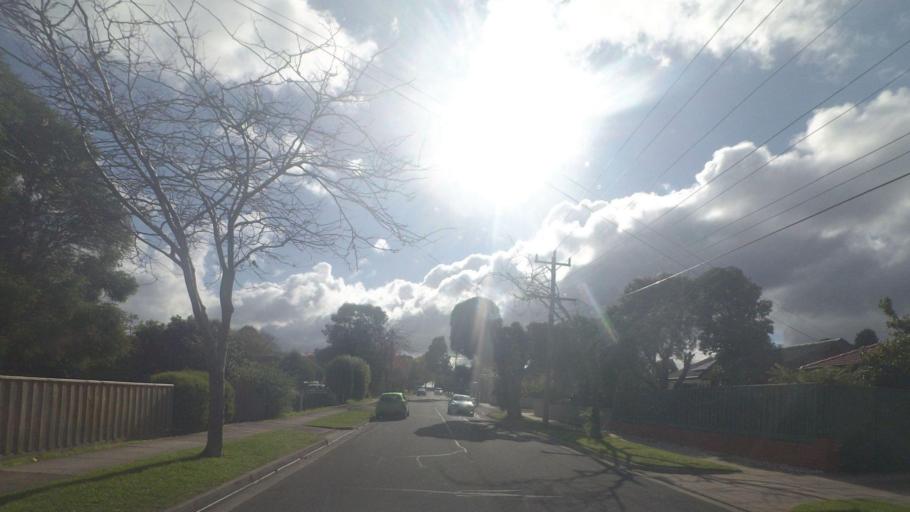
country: AU
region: Victoria
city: Forest Hill
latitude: -37.8392
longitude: 145.1836
